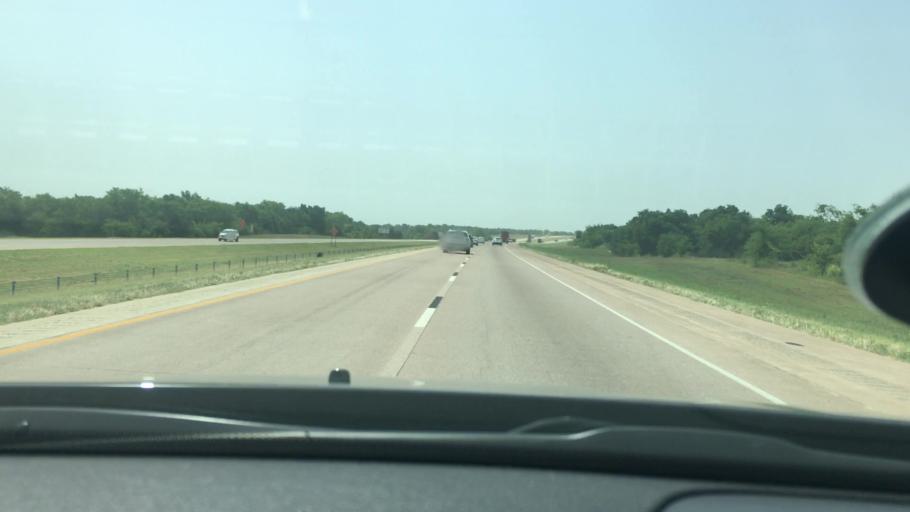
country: US
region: Oklahoma
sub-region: Garvin County
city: Pauls Valley
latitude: 34.6955
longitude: -97.2361
